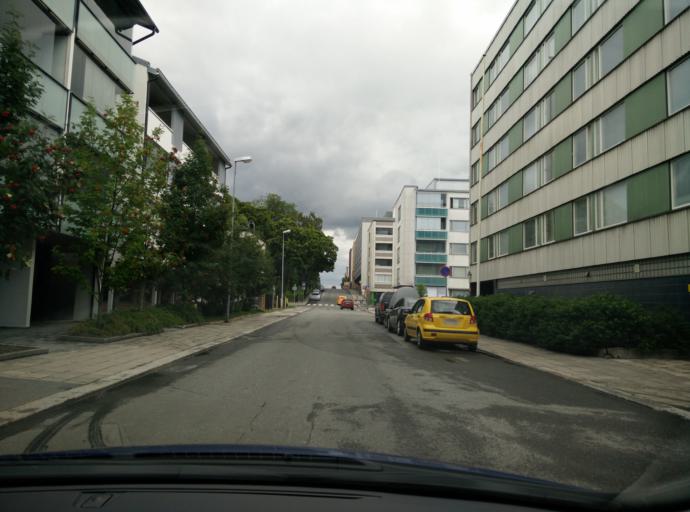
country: FI
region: Haeme
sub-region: Haemeenlinna
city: Haemeenlinna
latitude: 60.9973
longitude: 24.4615
